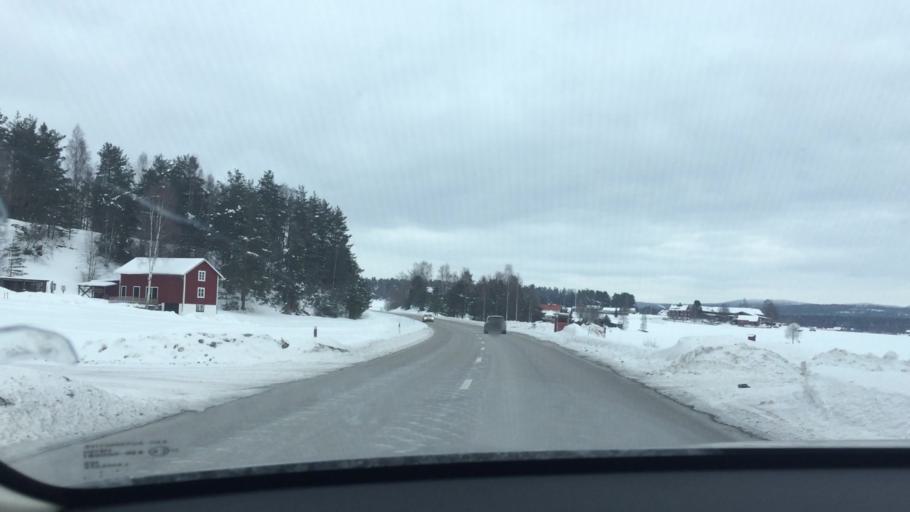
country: SE
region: Dalarna
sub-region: Faluns Kommun
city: Svardsjo
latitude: 60.6297
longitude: 15.8306
